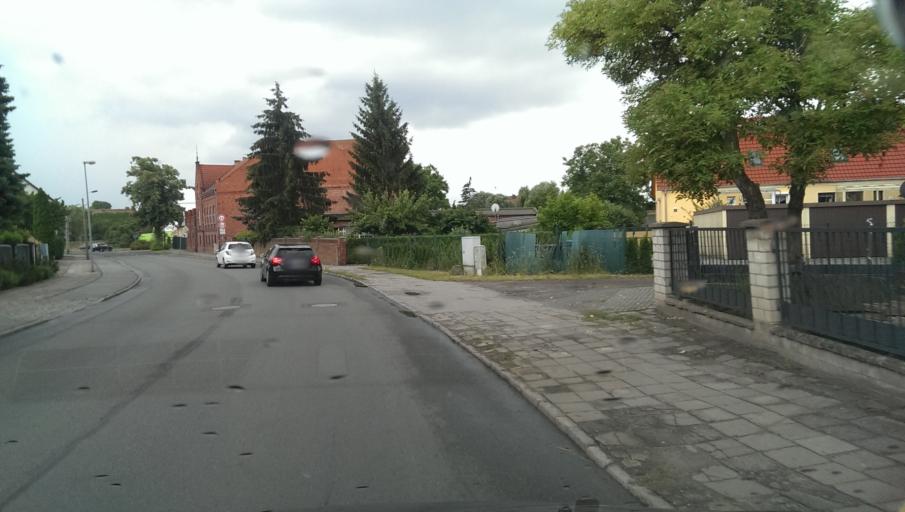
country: DE
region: Brandenburg
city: Rathenow
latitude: 52.6139
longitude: 12.3322
